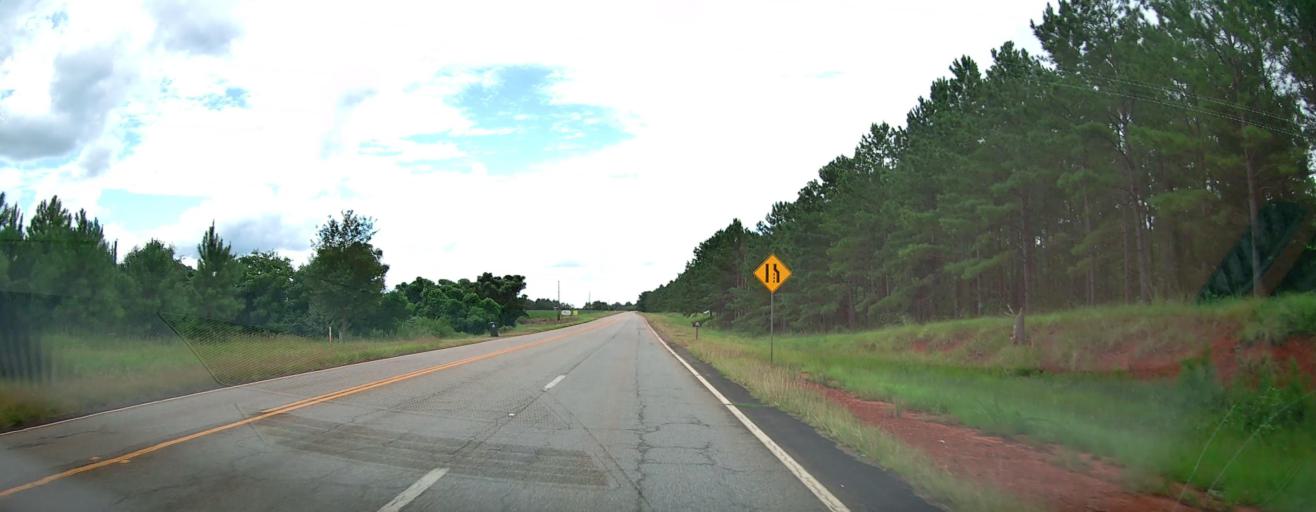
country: US
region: Georgia
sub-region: Marion County
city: Buena Vista
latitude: 32.2924
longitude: -84.4558
